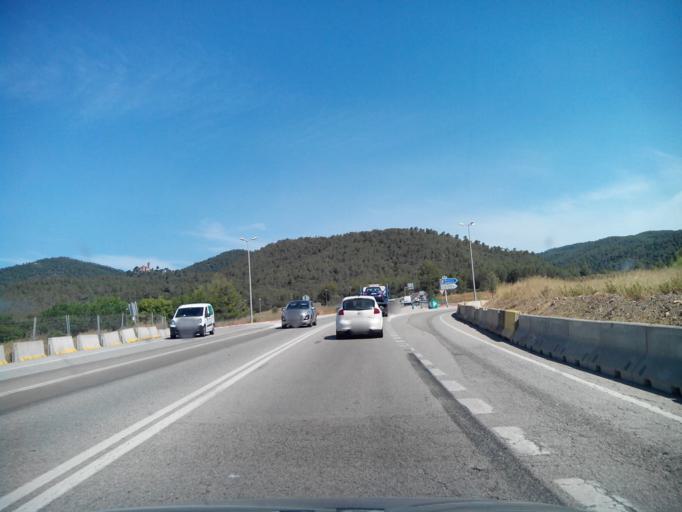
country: ES
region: Catalonia
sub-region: Provincia de Barcelona
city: Viladecavalls
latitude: 41.5632
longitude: 1.9661
